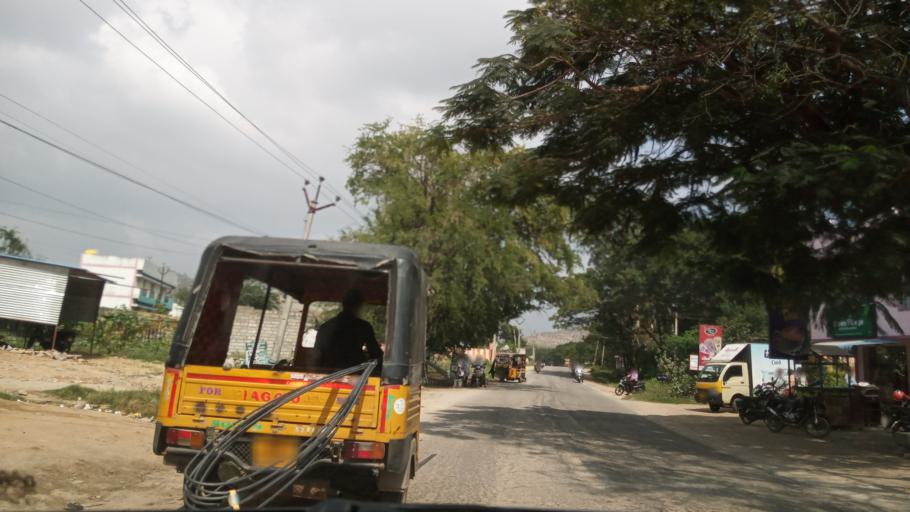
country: IN
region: Andhra Pradesh
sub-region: Chittoor
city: Madanapalle
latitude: 13.5716
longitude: 78.5165
